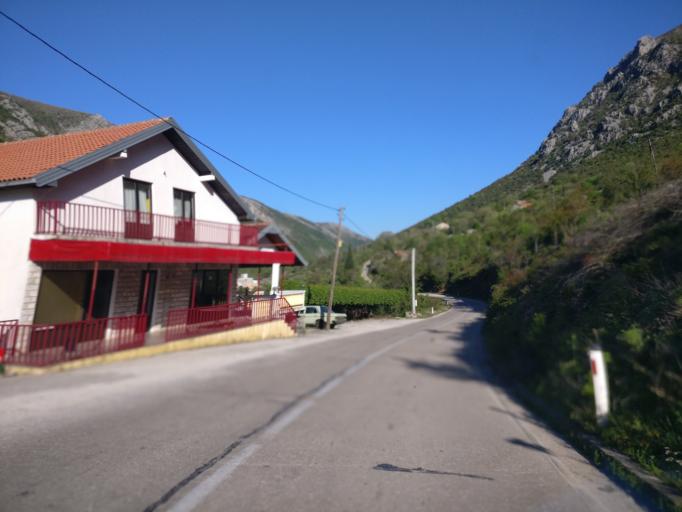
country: BA
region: Federation of Bosnia and Herzegovina
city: Stolac
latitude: 43.0770
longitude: 18.0231
